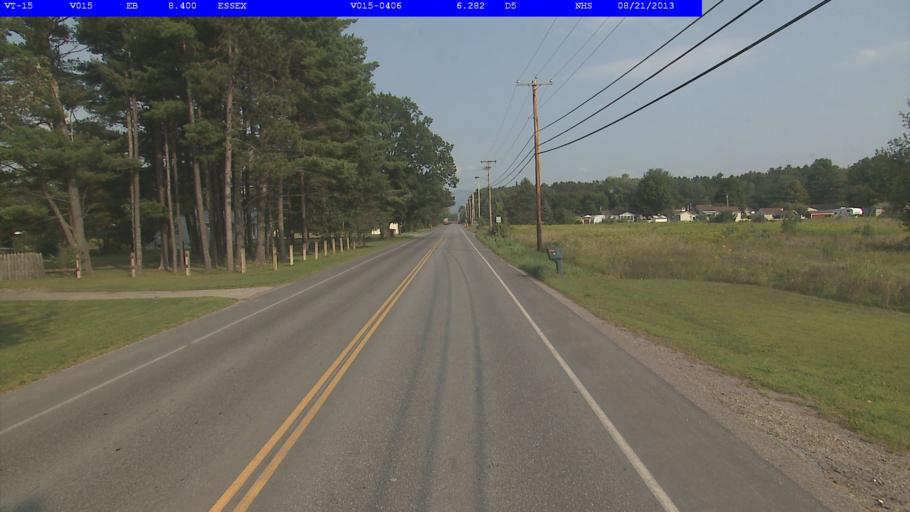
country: US
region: Vermont
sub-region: Chittenden County
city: Jericho
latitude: 44.5058
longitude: -73.0432
